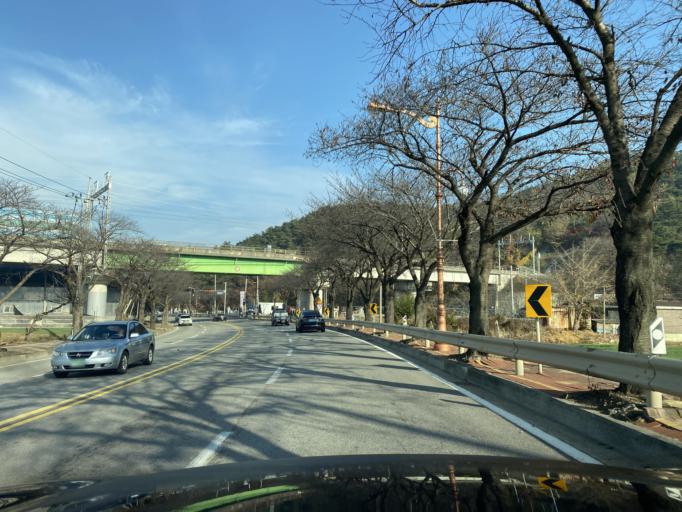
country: KR
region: Chungcheongnam-do
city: Yesan
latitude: 36.7355
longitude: 126.8622
